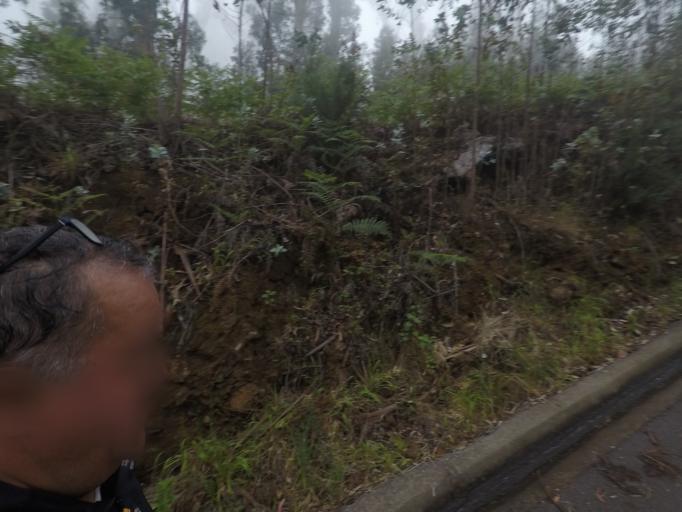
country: PT
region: Madeira
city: Ponta do Sol
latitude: 32.7113
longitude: -17.0955
